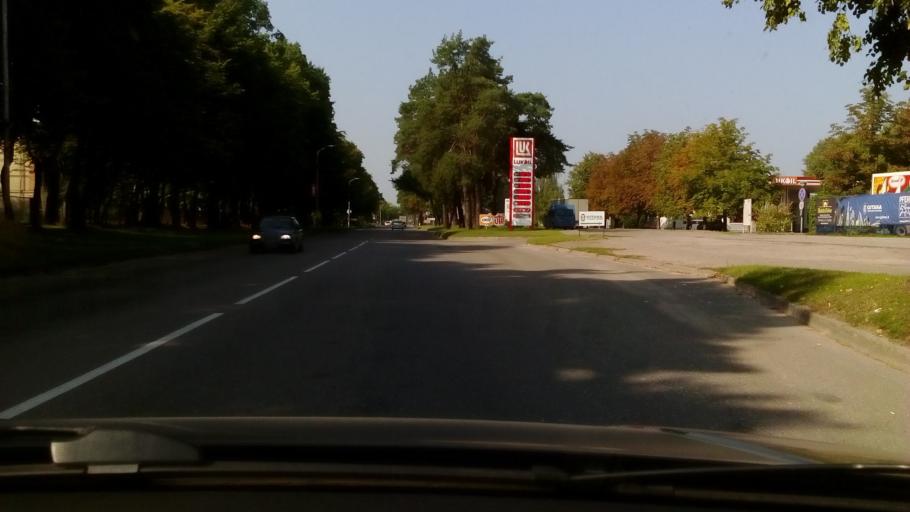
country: LT
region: Alytaus apskritis
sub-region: Alytus
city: Alytus
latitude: 54.3839
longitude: 24.0512
